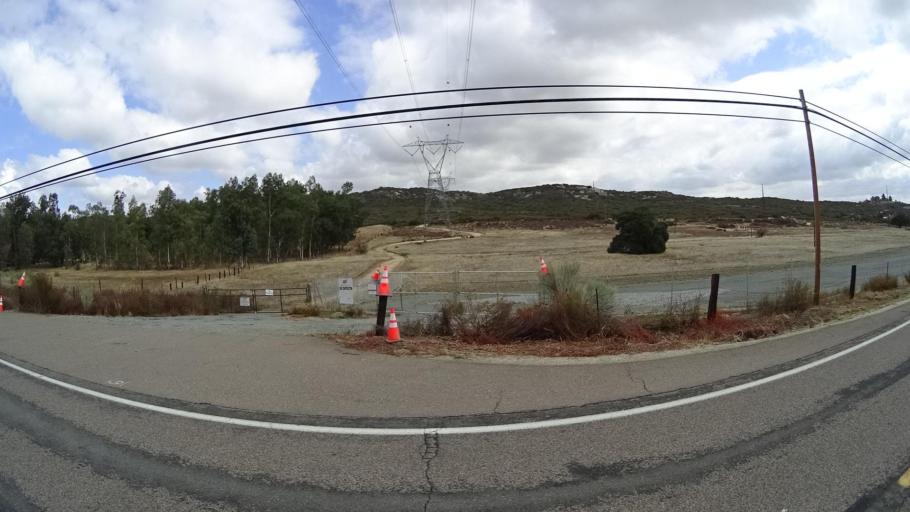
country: US
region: California
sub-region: San Diego County
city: Campo
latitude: 32.6559
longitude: -116.4877
